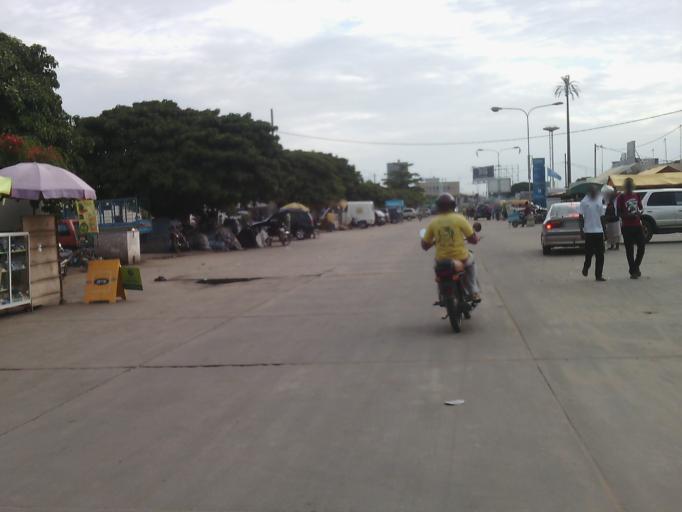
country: BJ
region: Littoral
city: Cotonou
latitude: 6.3847
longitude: 2.3808
